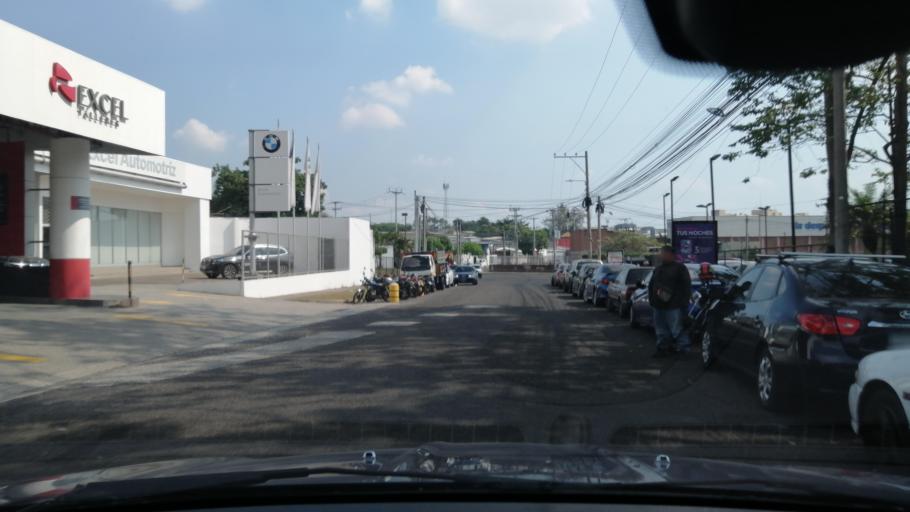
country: SV
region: San Salvador
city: San Salvador
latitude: 13.7050
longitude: -89.2166
